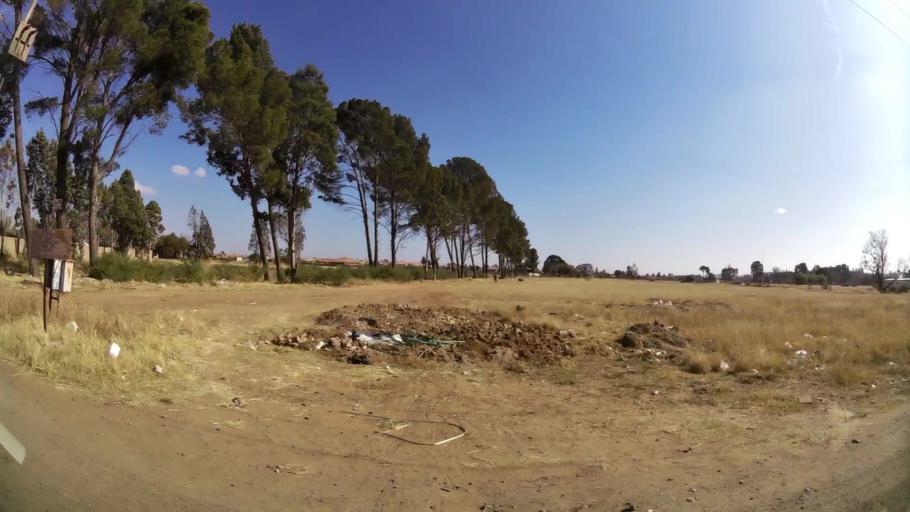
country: ZA
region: Orange Free State
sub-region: Mangaung Metropolitan Municipality
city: Bloemfontein
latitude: -29.1406
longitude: 26.2746
